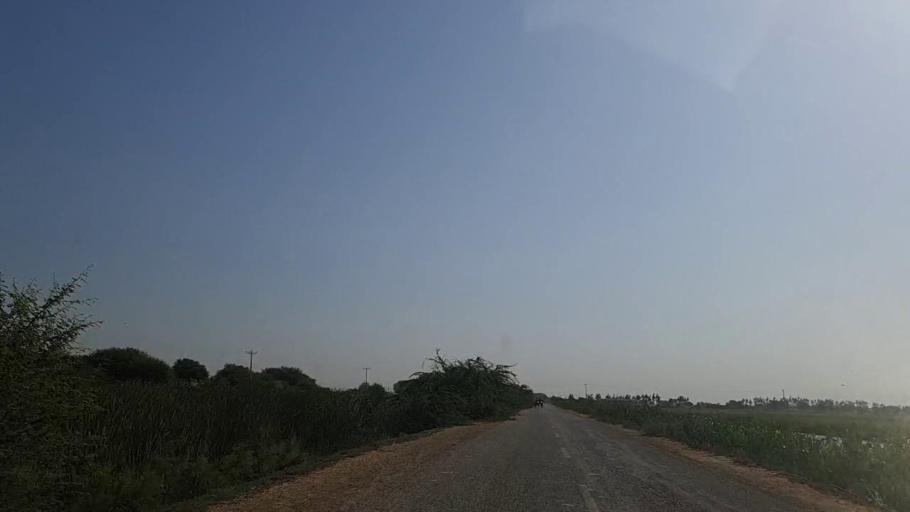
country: PK
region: Sindh
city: Jati
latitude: 24.4954
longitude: 68.2750
